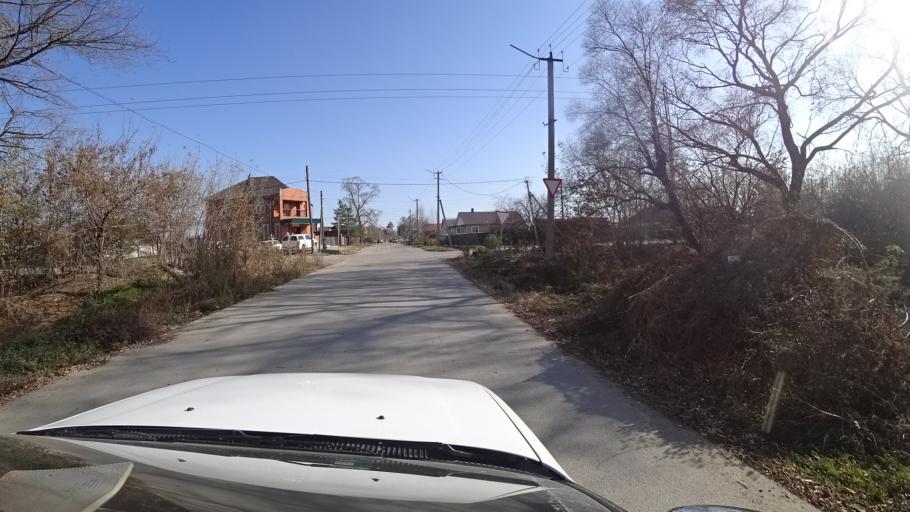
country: RU
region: Primorskiy
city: Dal'nerechensk
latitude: 45.9239
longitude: 133.7248
